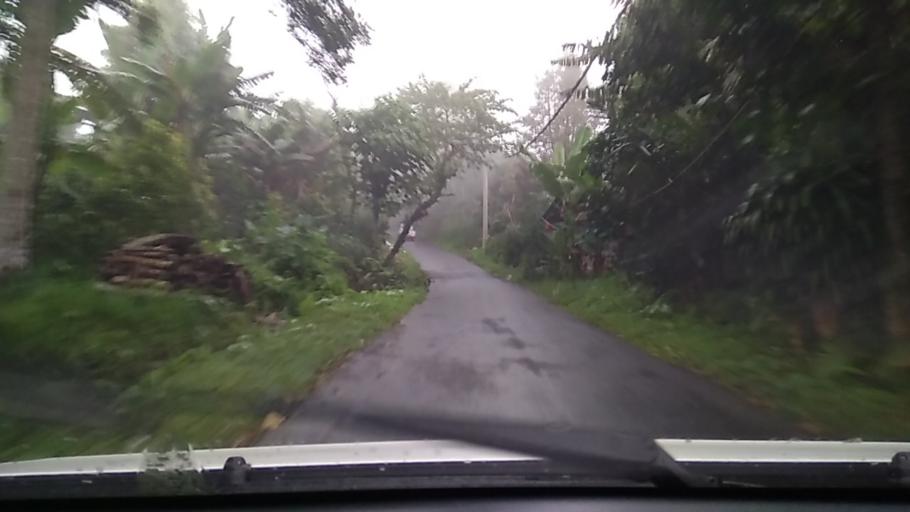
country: ID
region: Bali
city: Banjar Ambengan
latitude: -8.2033
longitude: 115.1736
